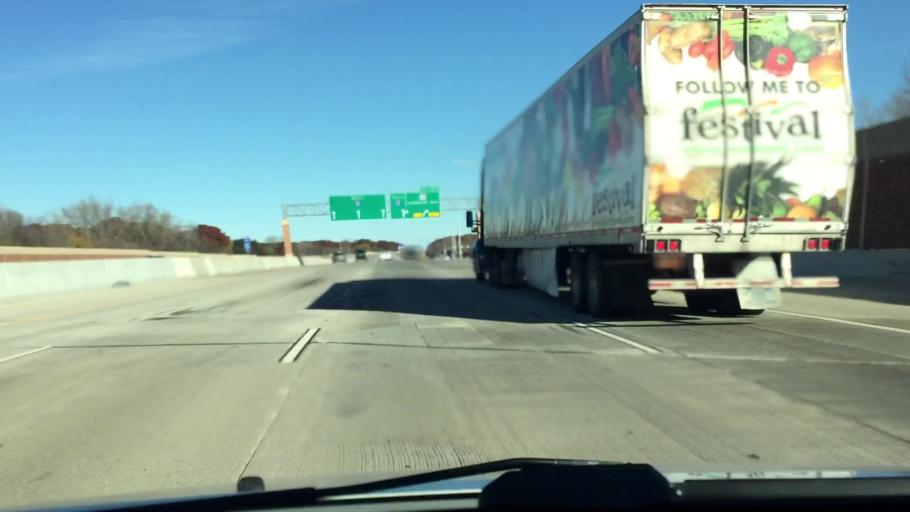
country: US
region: Wisconsin
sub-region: Brown County
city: Ashwaubenon
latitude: 44.5032
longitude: -88.0822
